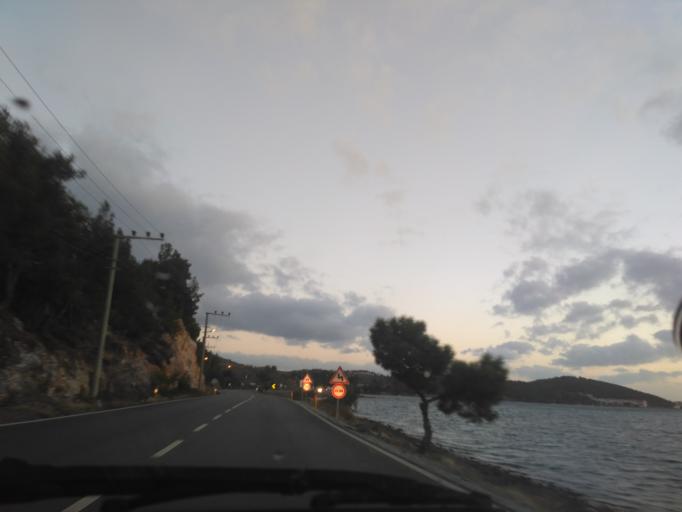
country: TR
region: Balikesir
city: Ayvalik
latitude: 39.2900
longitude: 26.6705
